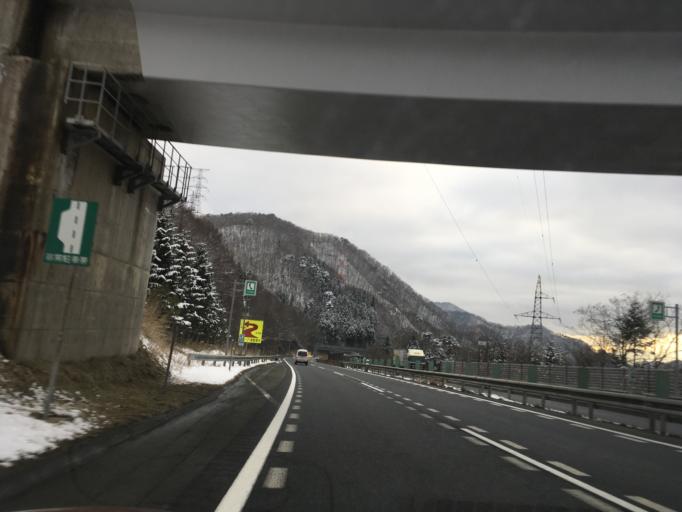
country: JP
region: Yamagata
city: Yamagata-shi
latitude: 38.2256
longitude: 140.4480
